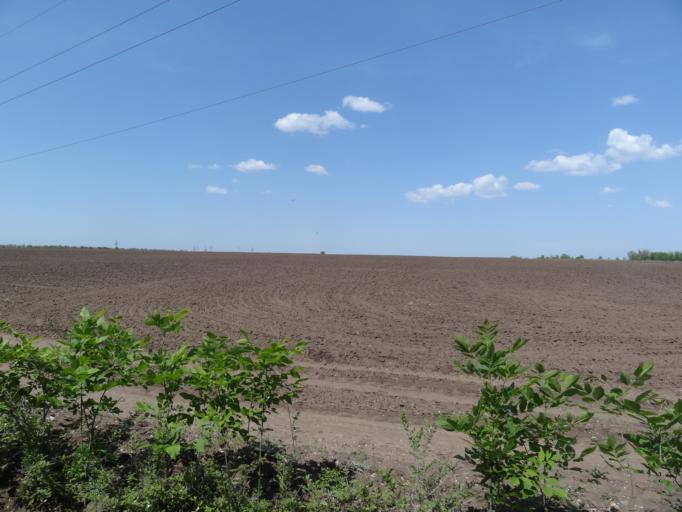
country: RU
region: Saratov
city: Privolzhskiy
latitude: 51.3461
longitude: 46.1698
